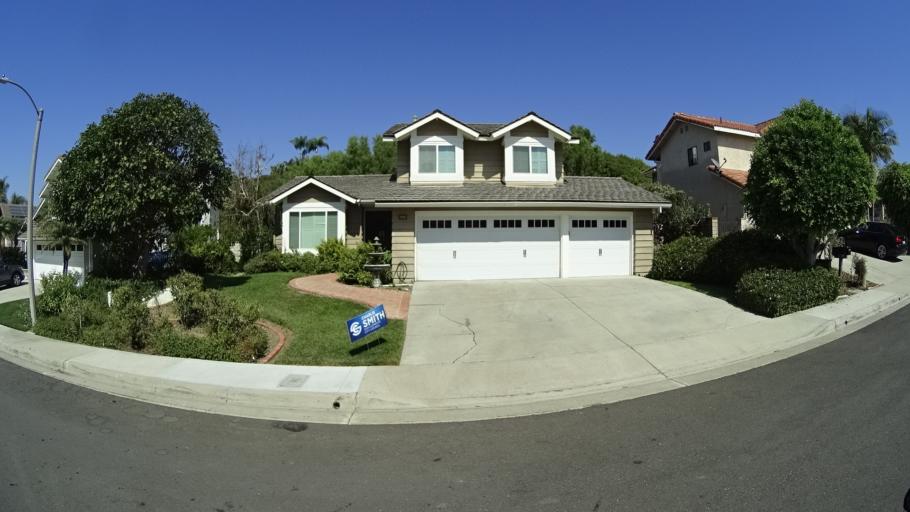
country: US
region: California
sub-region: Orange County
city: San Clemente
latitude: 33.4494
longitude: -117.6351
